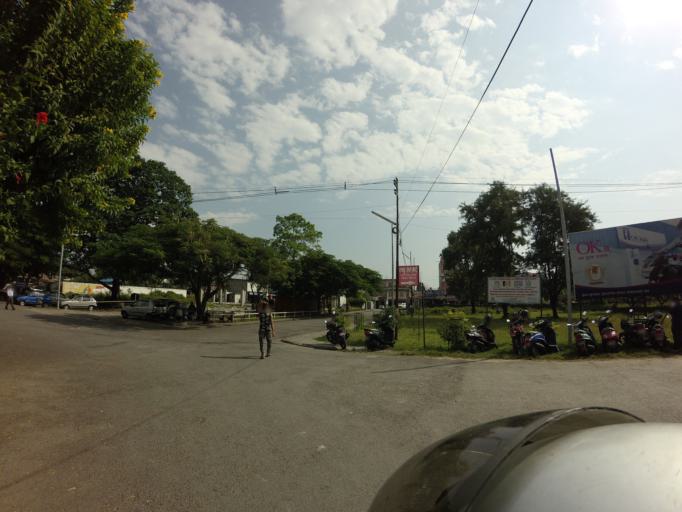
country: NP
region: Western Region
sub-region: Gandaki Zone
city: Pokhara
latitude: 28.2122
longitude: 83.9979
